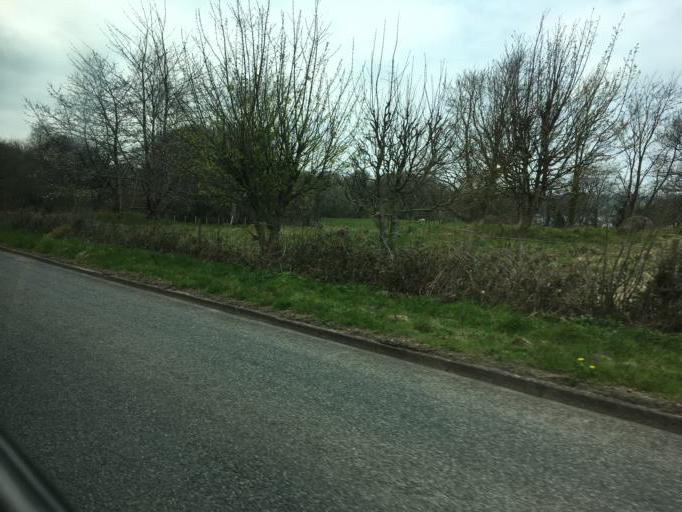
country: GB
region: Wales
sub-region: Gwynedd
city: Y Felinheli
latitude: 53.1755
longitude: -4.2231
